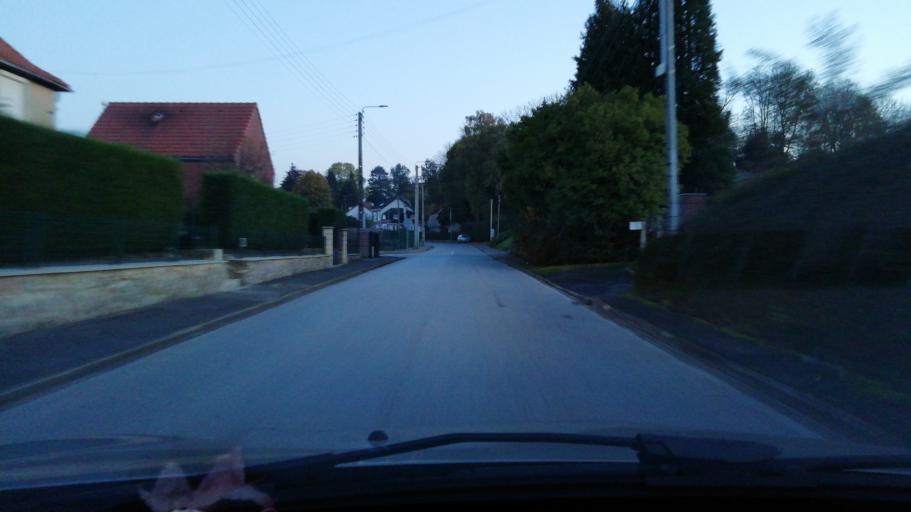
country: FR
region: Nord-Pas-de-Calais
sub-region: Departement du Nord
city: Marpent
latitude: 50.2882
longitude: 4.0848
